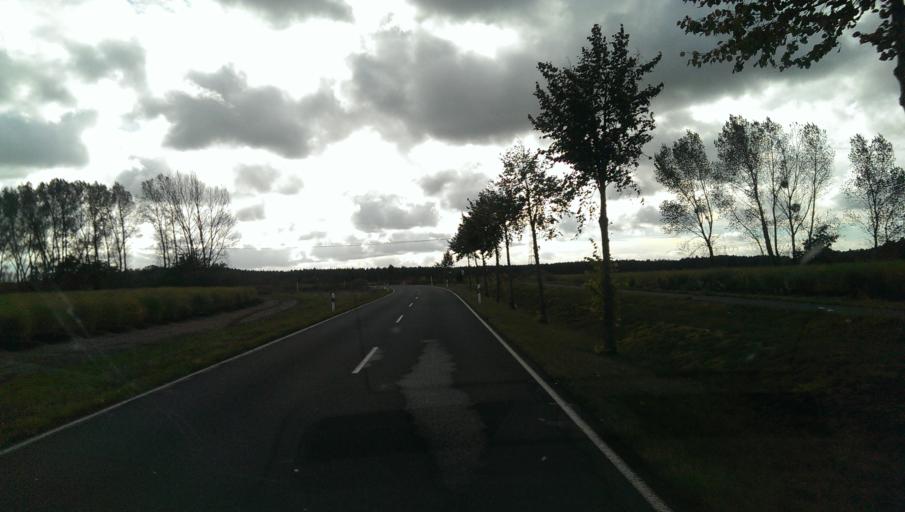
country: DE
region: Brandenburg
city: Luckenwalde
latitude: 52.1530
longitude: 13.1839
